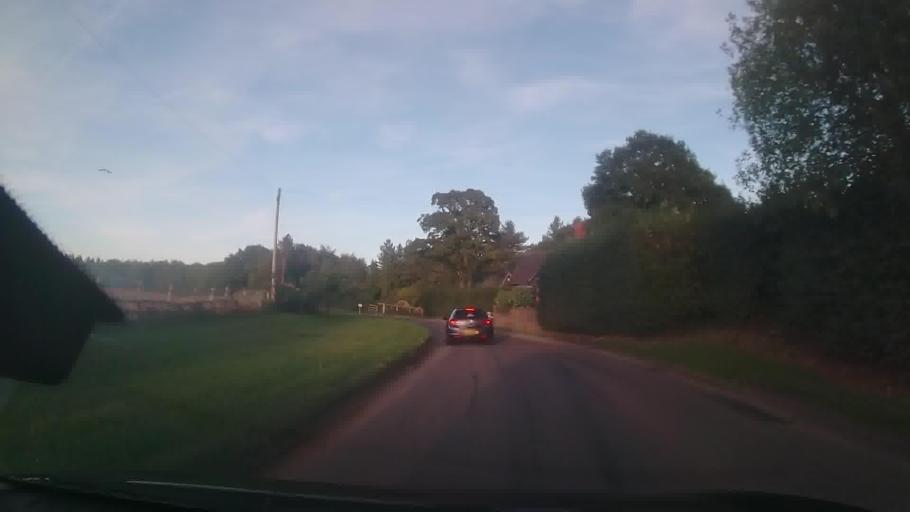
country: GB
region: England
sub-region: Shropshire
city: Bicton
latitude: 52.7583
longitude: -2.8176
